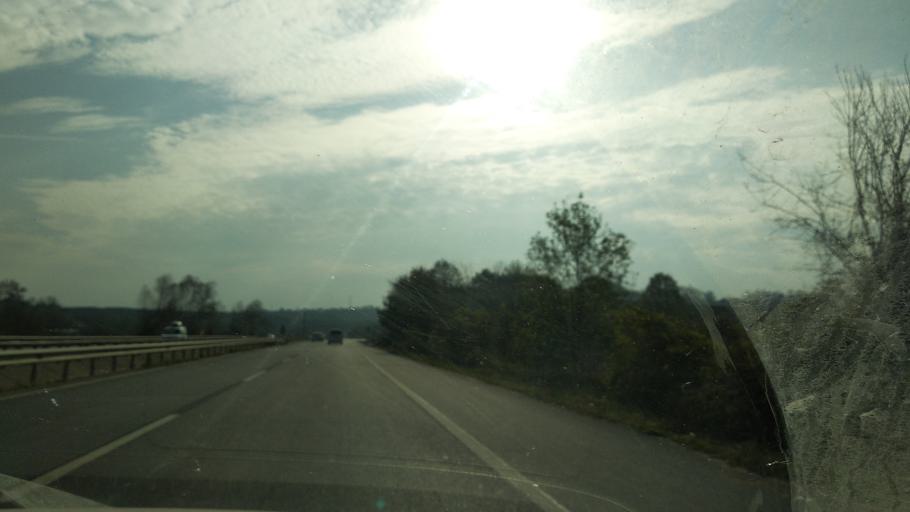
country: TR
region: Sakarya
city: Karasu
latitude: 41.0571
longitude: 30.6361
